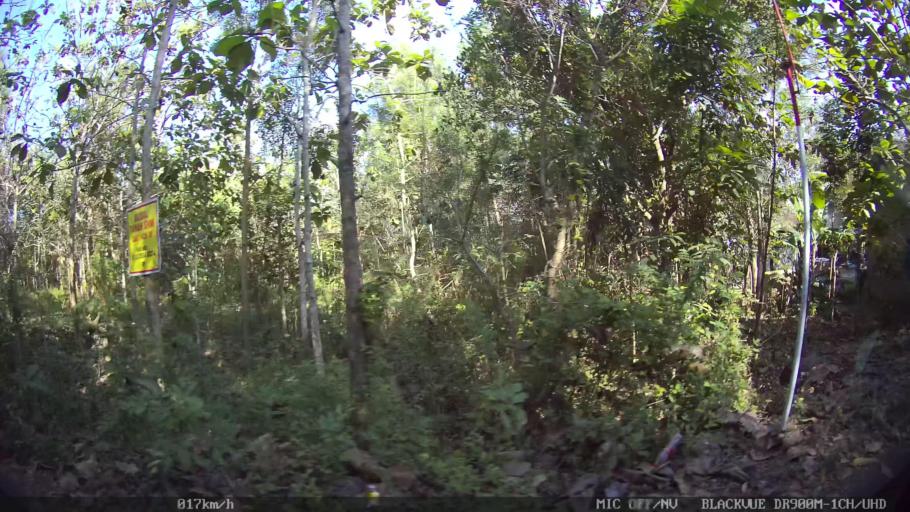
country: ID
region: Daerah Istimewa Yogyakarta
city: Kasihan
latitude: -7.8346
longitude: 110.2864
